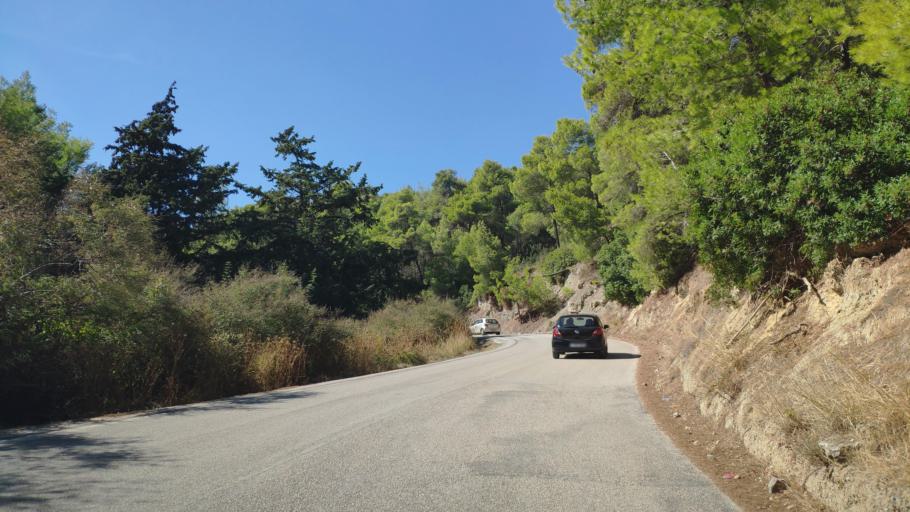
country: GR
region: Attica
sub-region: Nomarchia Anatolikis Attikis
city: Kouvaras
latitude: 37.8401
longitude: 23.9961
